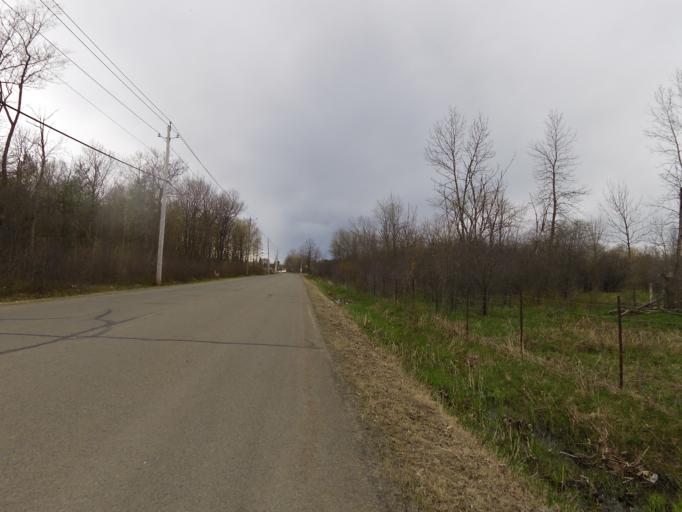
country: CA
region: Ontario
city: Hawkesbury
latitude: 45.6254
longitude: -74.5821
